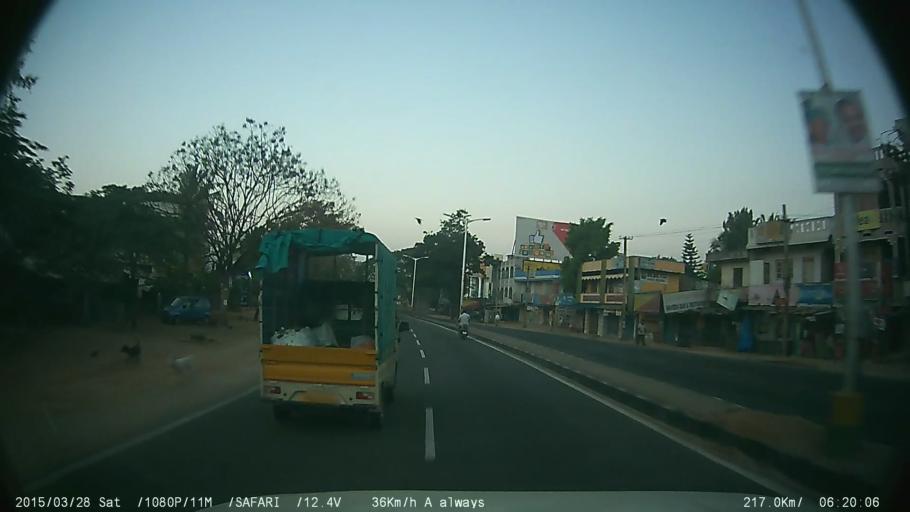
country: IN
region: Karnataka
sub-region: Ramanagara
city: Ramanagaram
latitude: 12.7320
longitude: 77.2896
